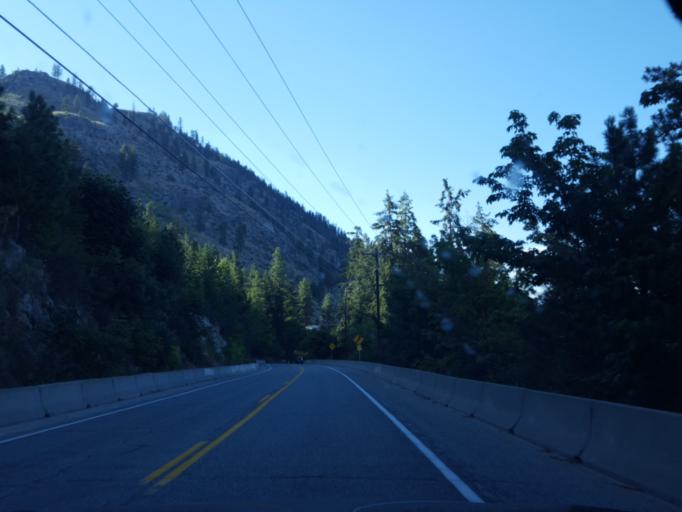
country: US
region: Washington
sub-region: Chelan County
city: Granite Falls
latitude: 47.8879
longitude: -120.2137
